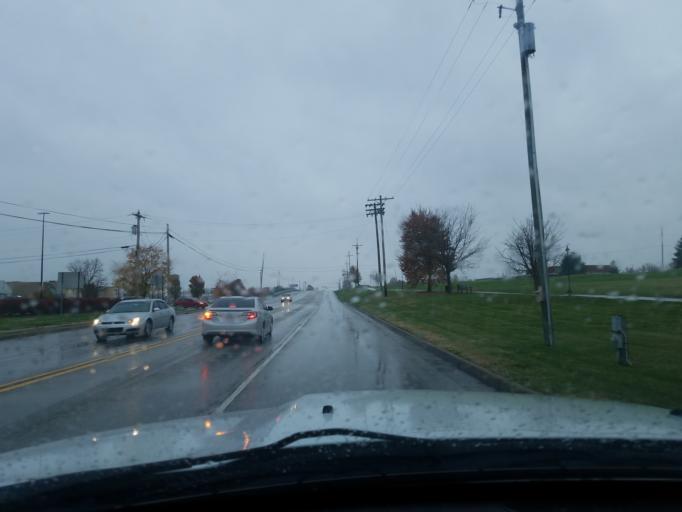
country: US
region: Indiana
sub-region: Floyd County
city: New Albany
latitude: 38.3216
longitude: -85.8200
